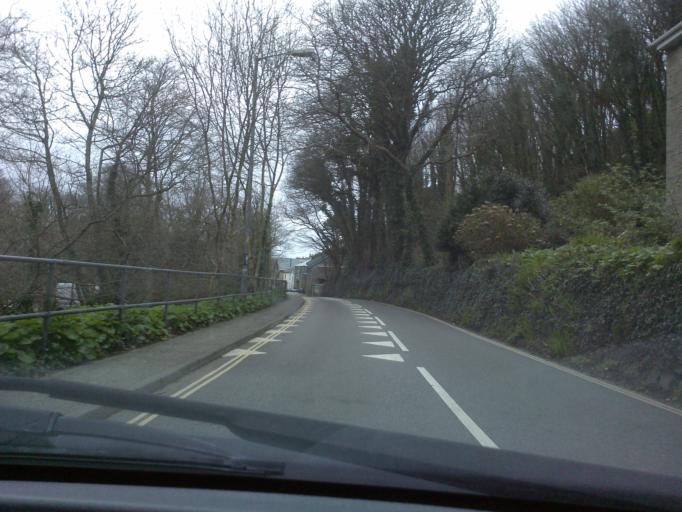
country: GB
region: England
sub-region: Cornwall
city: Penzance
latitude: 50.1081
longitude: -5.5536
